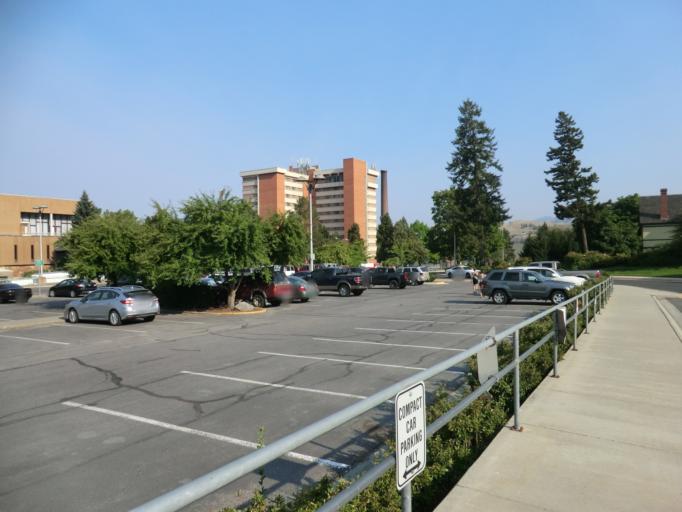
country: US
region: Montana
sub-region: Missoula County
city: Missoula
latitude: 46.8607
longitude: -113.9811
